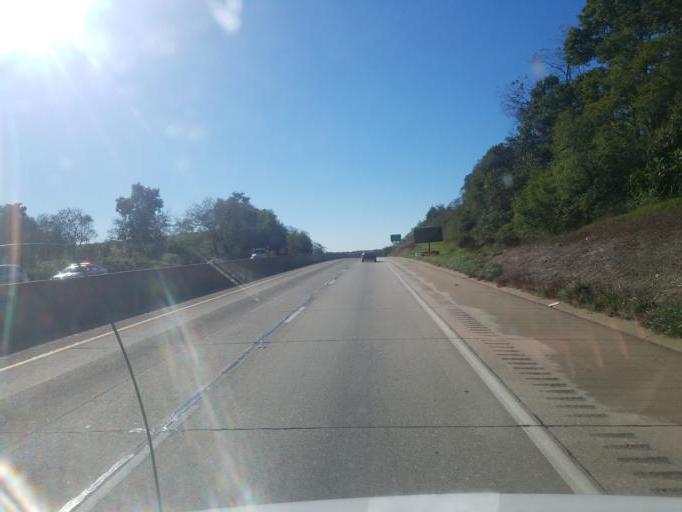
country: US
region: Pennsylvania
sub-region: Allegheny County
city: Enlow
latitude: 40.4381
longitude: -80.1960
